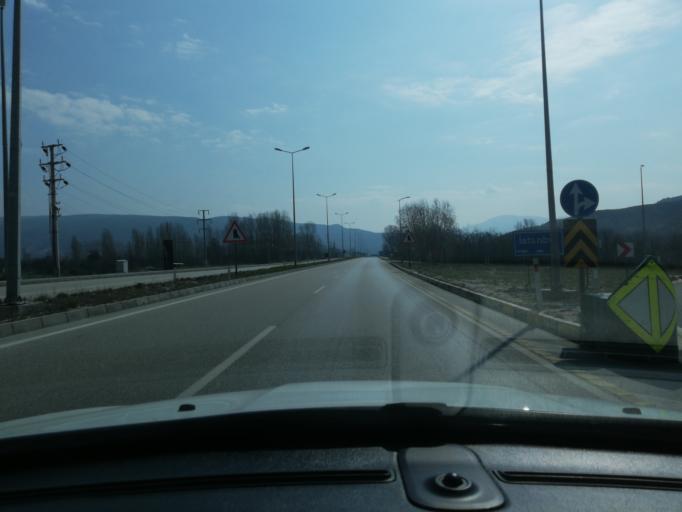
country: TR
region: Cankiri
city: Ilgaz
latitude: 40.9081
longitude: 33.6356
